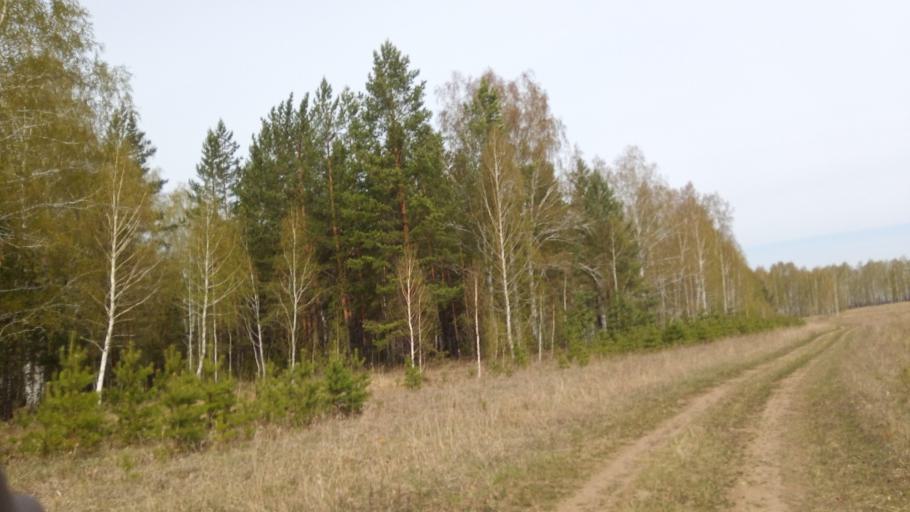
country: RU
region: Chelyabinsk
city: Timiryazevskiy
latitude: 55.0196
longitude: 60.8596
